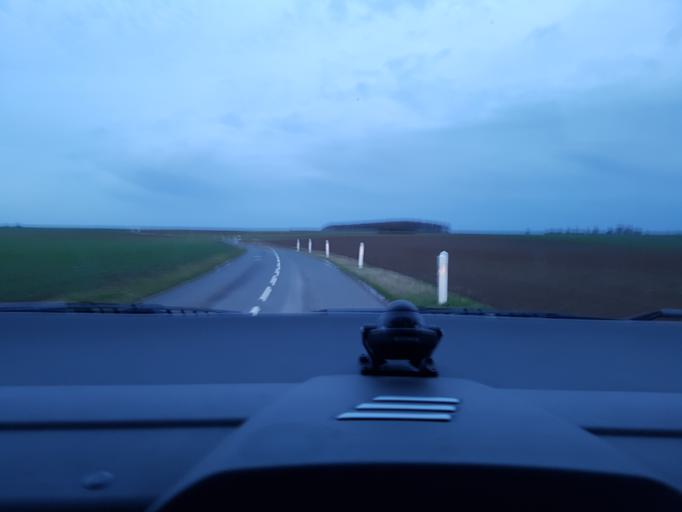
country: FR
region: Picardie
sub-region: Departement de la Somme
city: Beauquesne
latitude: 50.0267
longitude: 2.3906
